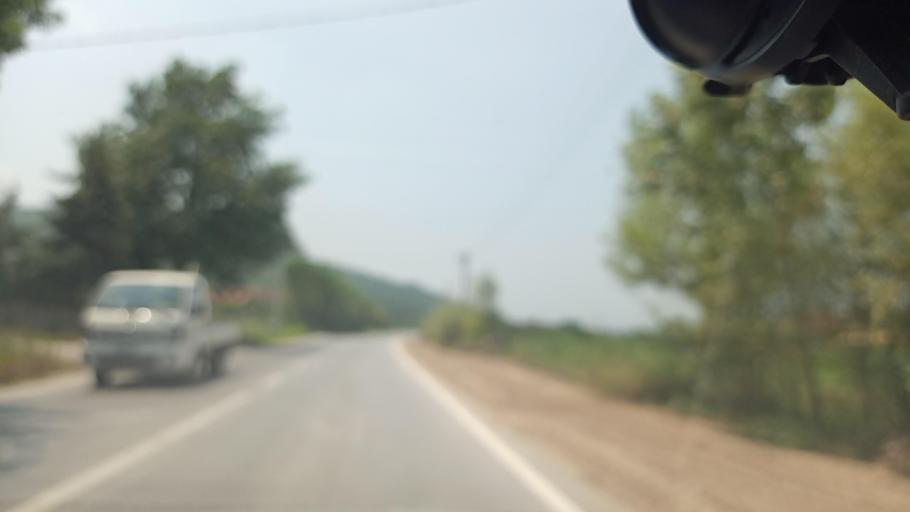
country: TR
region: Sakarya
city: Adapazari
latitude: 40.8389
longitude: 30.4113
